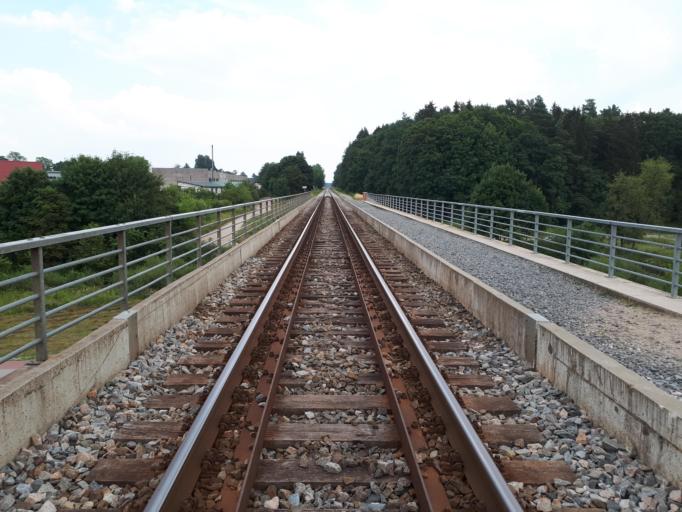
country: LT
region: Klaipedos apskritis
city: Silute
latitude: 55.3408
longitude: 21.4928
